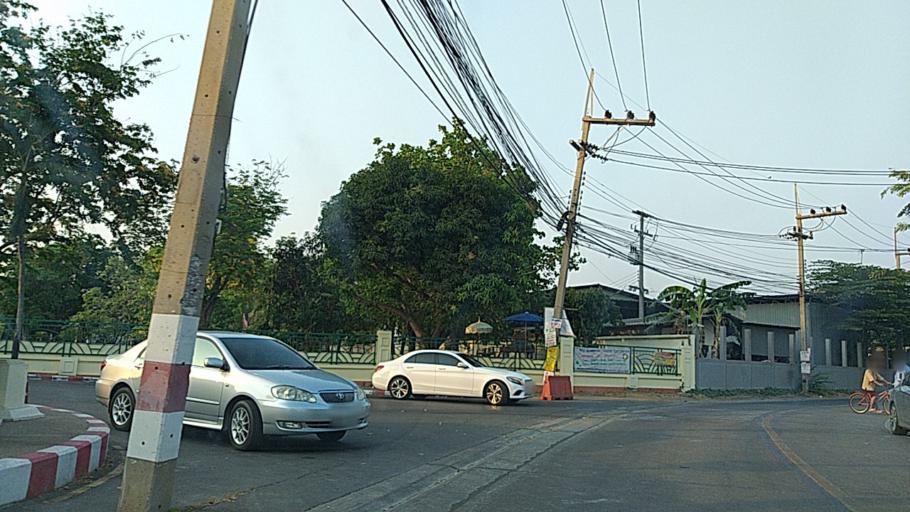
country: TH
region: Phra Nakhon Si Ayutthaya
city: Ban Bang Kadi Pathum Thani
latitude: 14.0011
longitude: 100.5642
